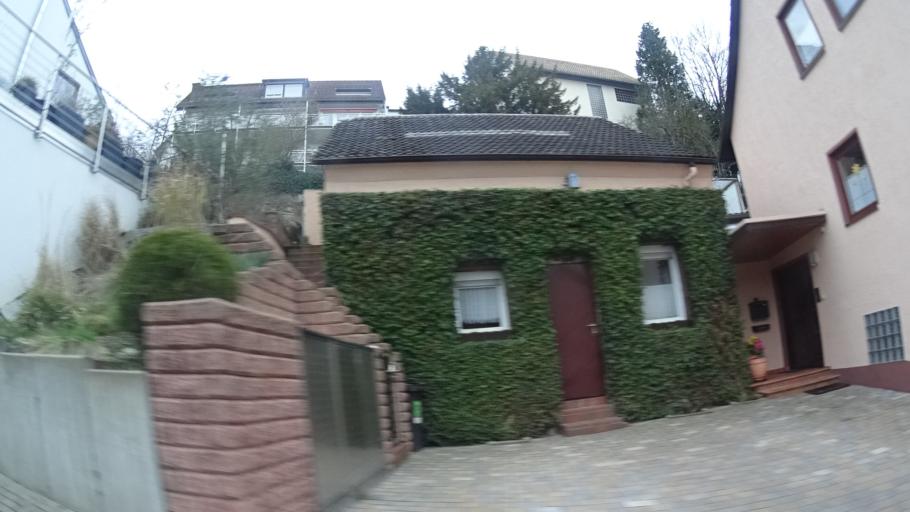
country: DE
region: Hesse
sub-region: Regierungsbezirk Darmstadt
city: Wiesbaden
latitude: 50.1144
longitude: 8.2732
